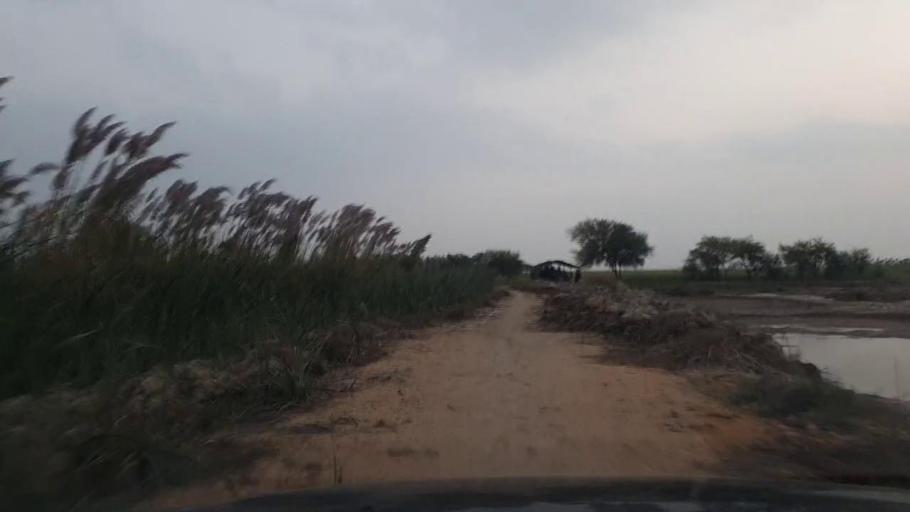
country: PK
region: Sindh
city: Jati
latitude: 24.5189
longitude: 68.3671
